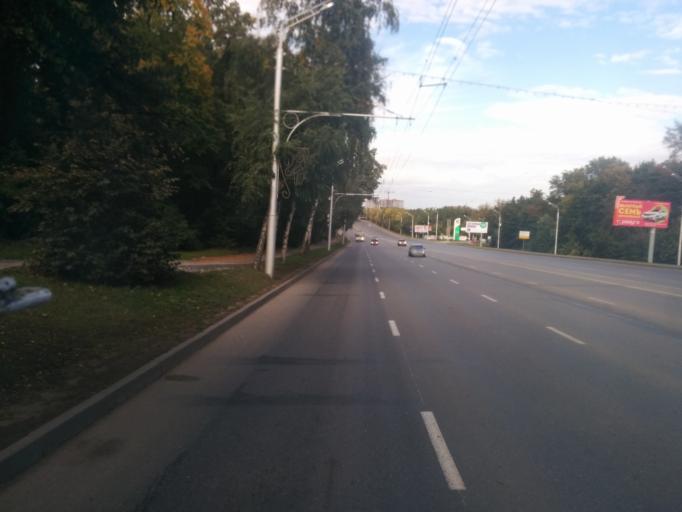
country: RU
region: Bashkortostan
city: Ufa
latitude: 54.8023
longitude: 56.0451
